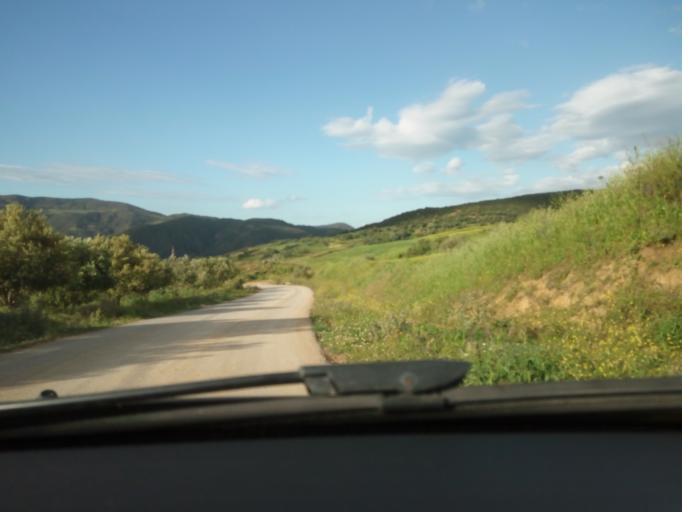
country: DZ
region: Tipaza
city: El Affroun
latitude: 36.3735
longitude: 2.4982
